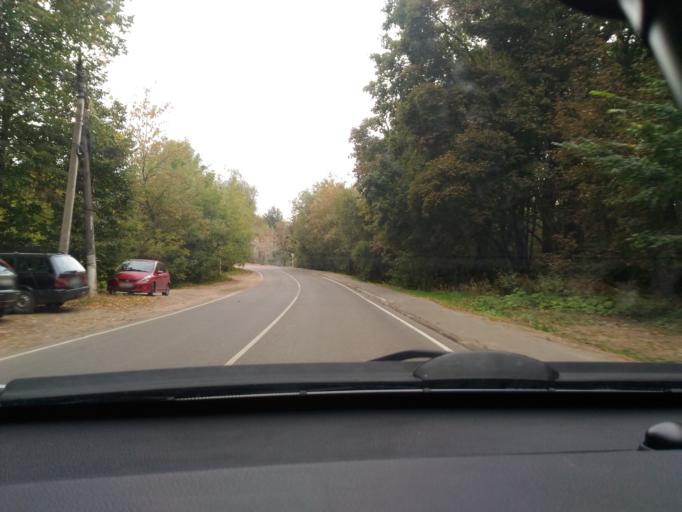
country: RU
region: Moskovskaya
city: Povarovo
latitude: 56.0800
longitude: 37.0597
